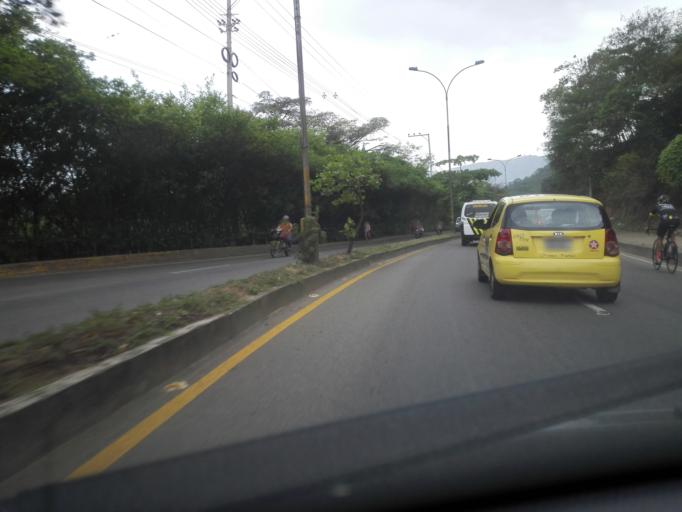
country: CO
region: Santander
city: Bucaramanga
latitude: 7.0893
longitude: -73.1314
